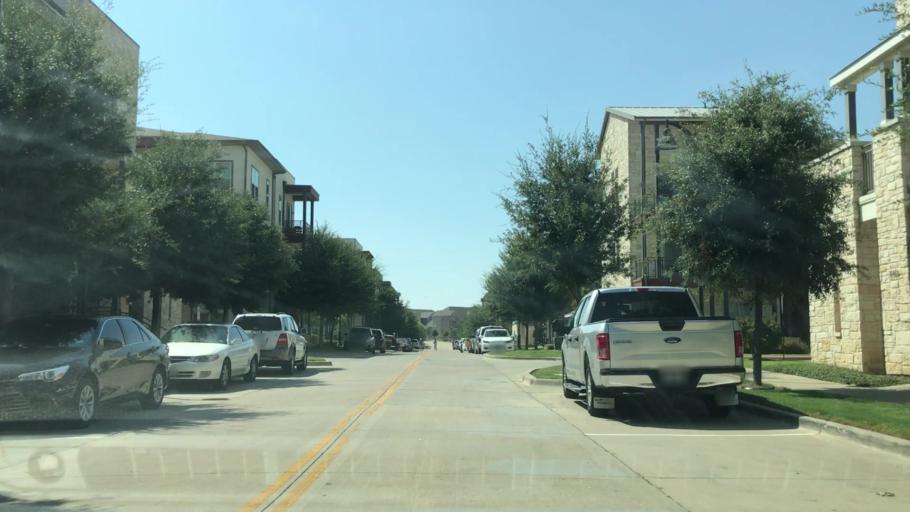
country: US
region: Texas
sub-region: Dallas County
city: Coppell
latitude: 32.9325
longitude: -96.9860
